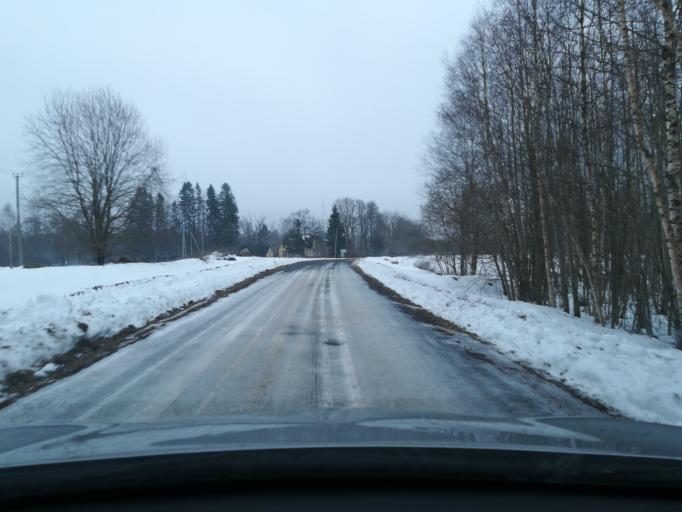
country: EE
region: Harju
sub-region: Loksa linn
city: Loksa
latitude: 59.4665
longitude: 25.7027
